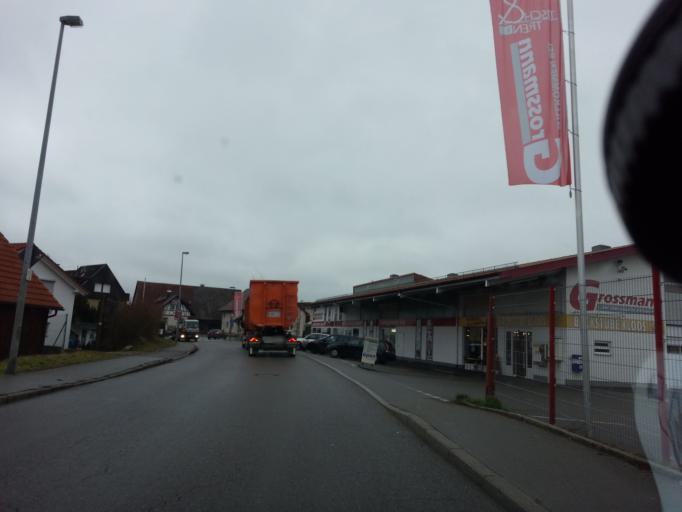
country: DE
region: Baden-Wuerttemberg
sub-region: Tuebingen Region
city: Oberteuringen
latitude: 47.6853
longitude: 9.4436
